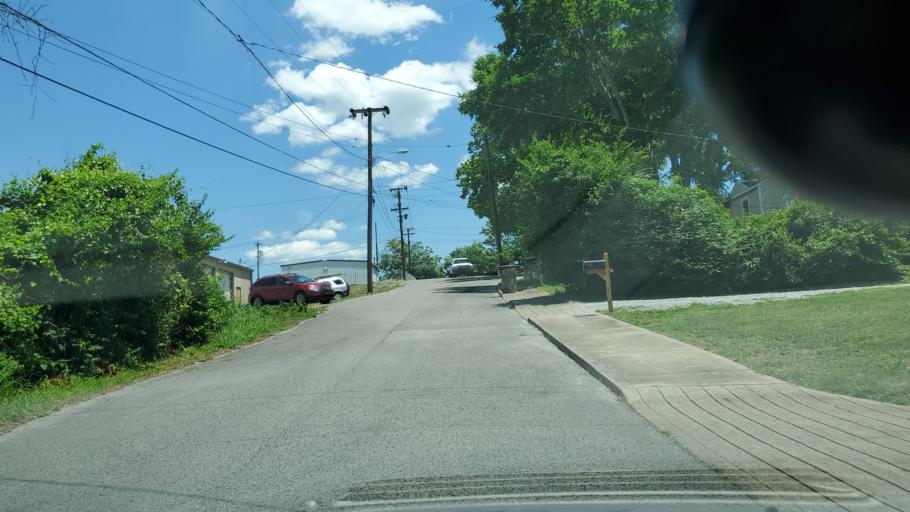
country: US
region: Tennessee
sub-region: Davidson County
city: Nashville
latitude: 36.1926
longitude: -86.7550
